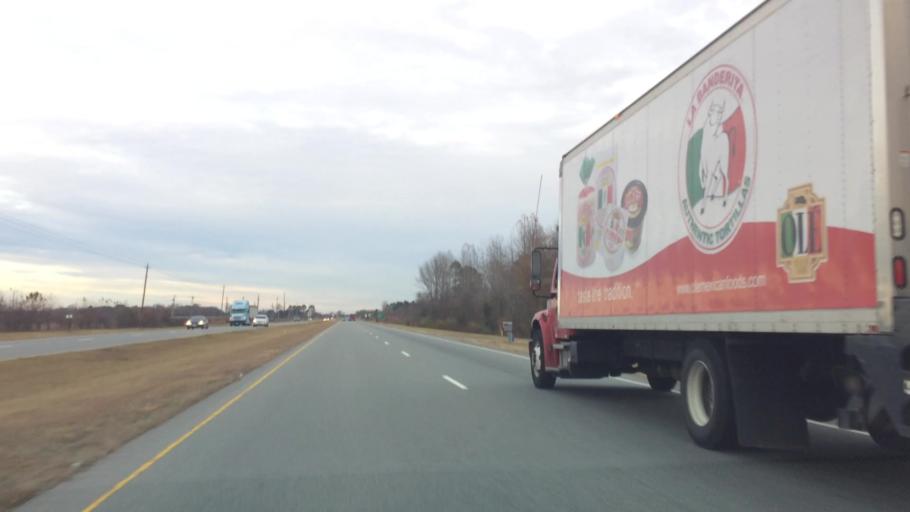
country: US
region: North Carolina
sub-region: Wayne County
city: Mount Olive
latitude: 35.1763
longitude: -78.0984
